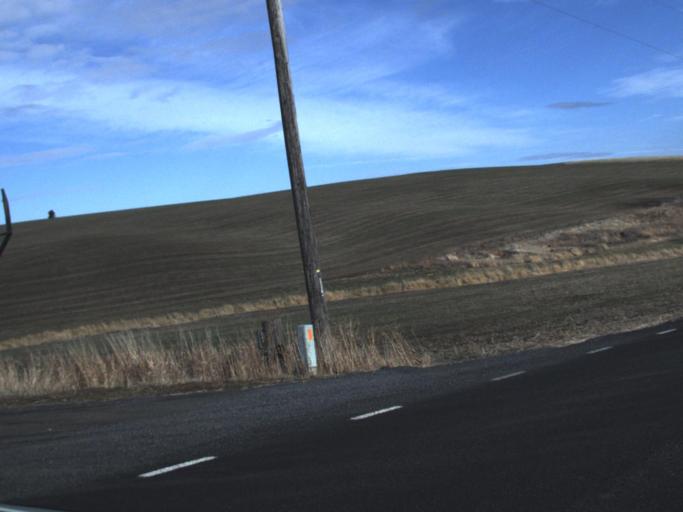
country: US
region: Washington
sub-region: Whitman County
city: Colfax
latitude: 46.9333
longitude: -117.2197
